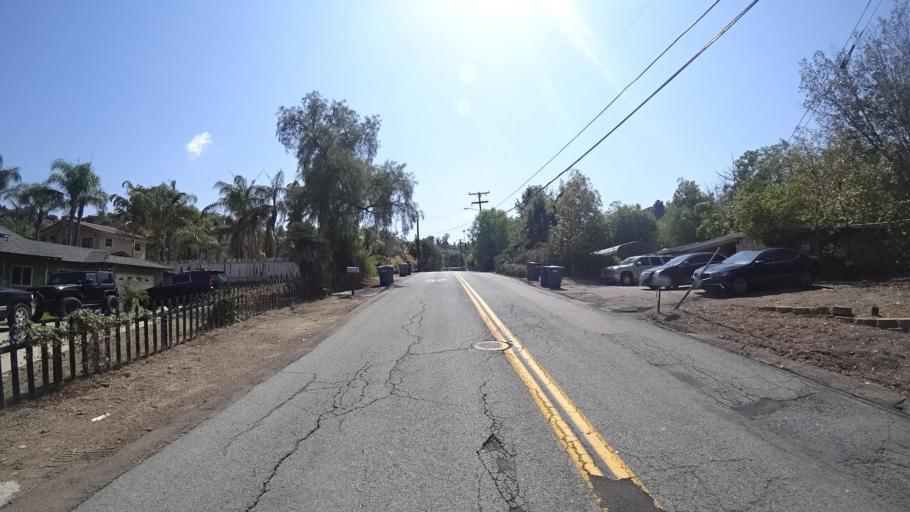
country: US
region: California
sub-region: San Diego County
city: Spring Valley
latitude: 32.7402
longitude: -116.9884
